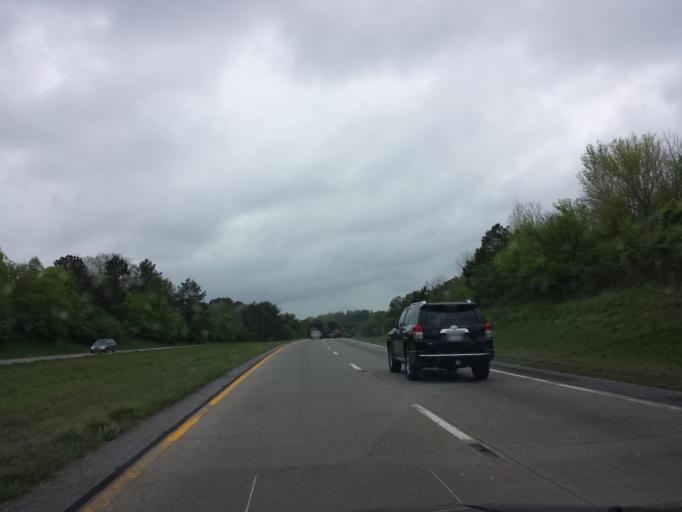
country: US
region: Georgia
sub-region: Pickens County
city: Jasper
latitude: 34.4104
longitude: -84.4250
